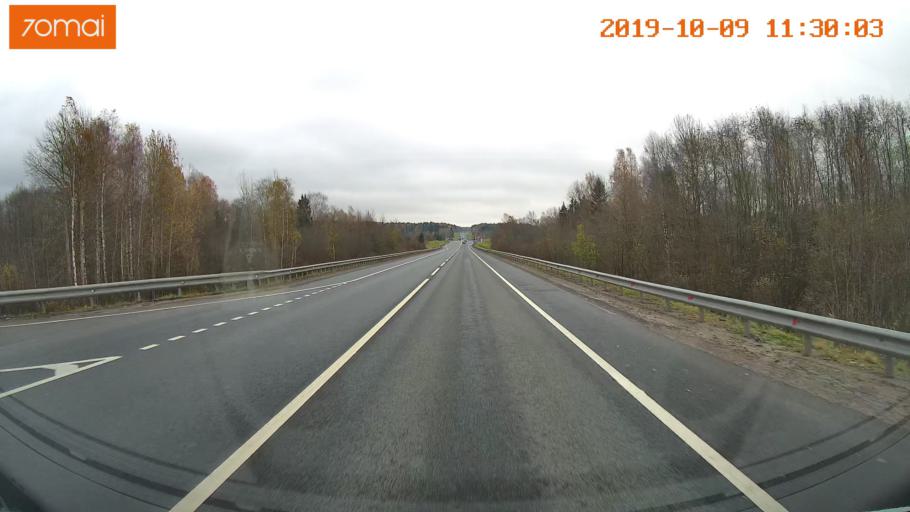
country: RU
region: Vologda
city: Vologda
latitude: 59.0570
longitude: 40.0669
